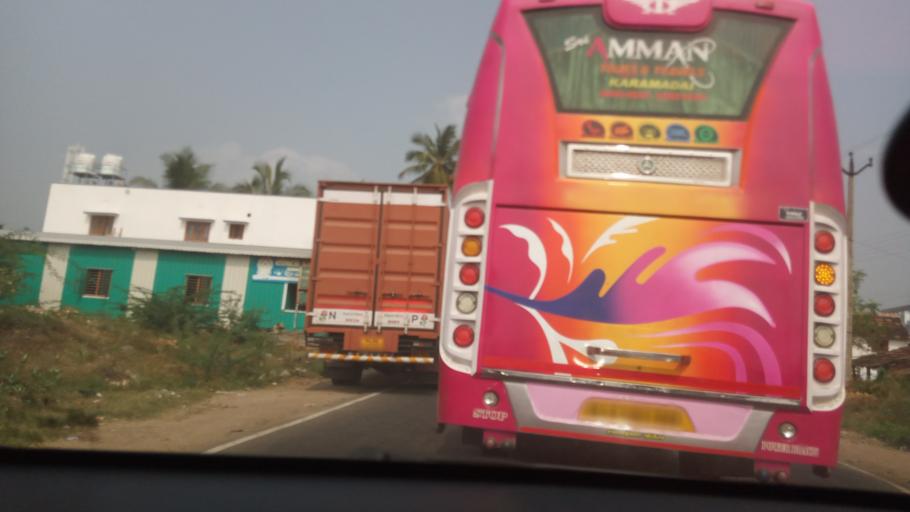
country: IN
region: Tamil Nadu
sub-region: Erode
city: Sathyamangalam
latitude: 11.5246
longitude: 77.1431
